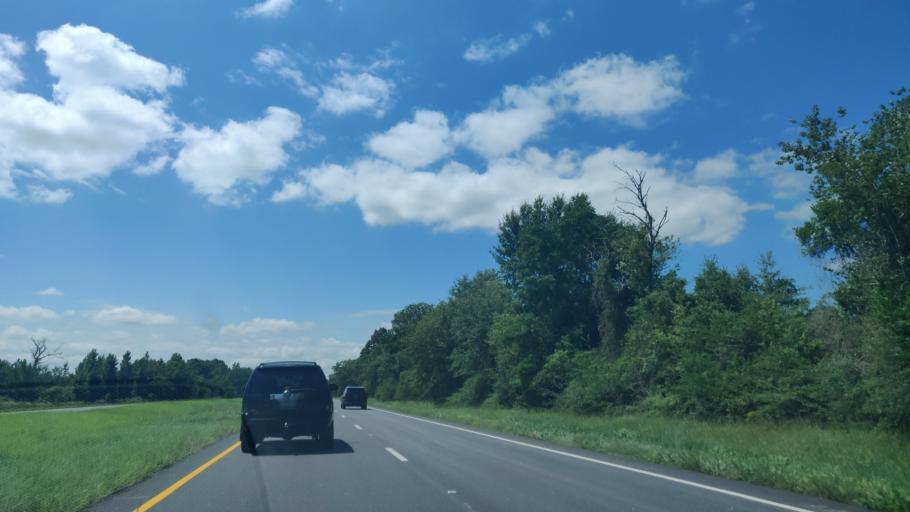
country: US
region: Georgia
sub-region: Stewart County
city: Richland
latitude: 32.1183
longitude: -84.6781
